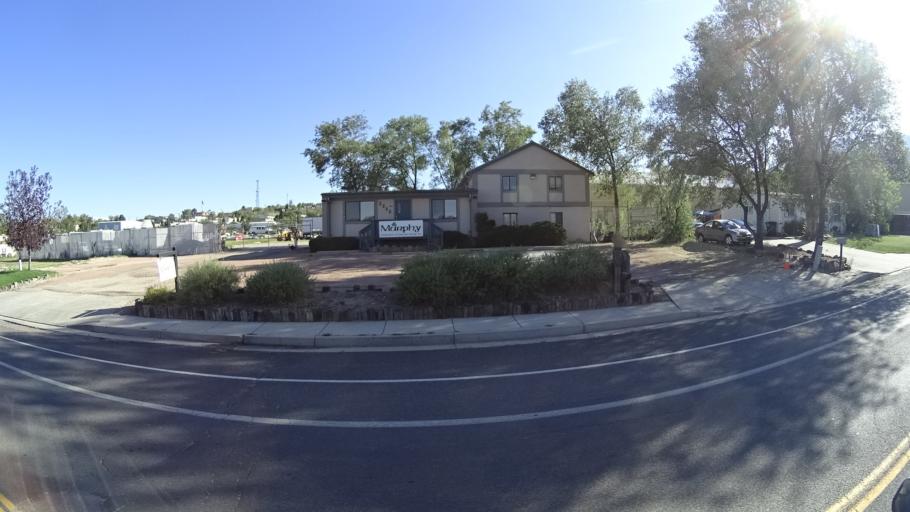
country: US
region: Colorado
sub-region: El Paso County
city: Colorado Springs
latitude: 38.8373
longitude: -104.8631
